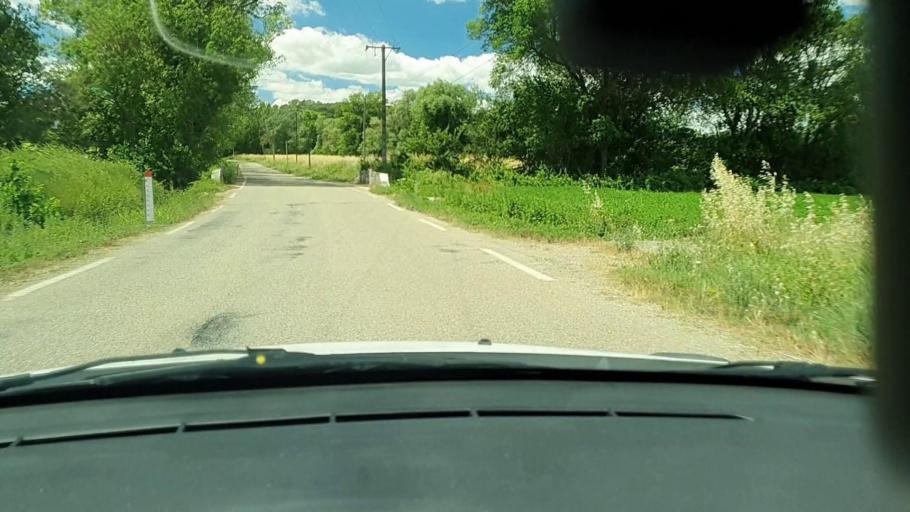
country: FR
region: Languedoc-Roussillon
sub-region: Departement du Gard
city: Blauzac
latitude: 43.9499
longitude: 4.3840
